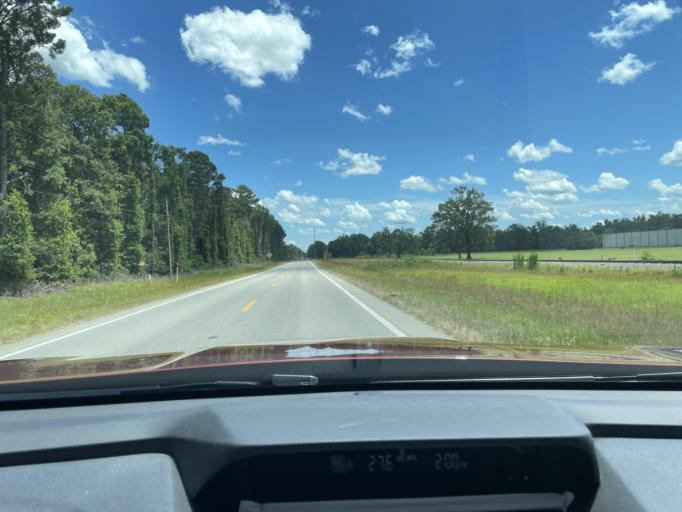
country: US
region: Arkansas
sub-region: Drew County
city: Monticello
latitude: 33.6166
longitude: -91.7452
